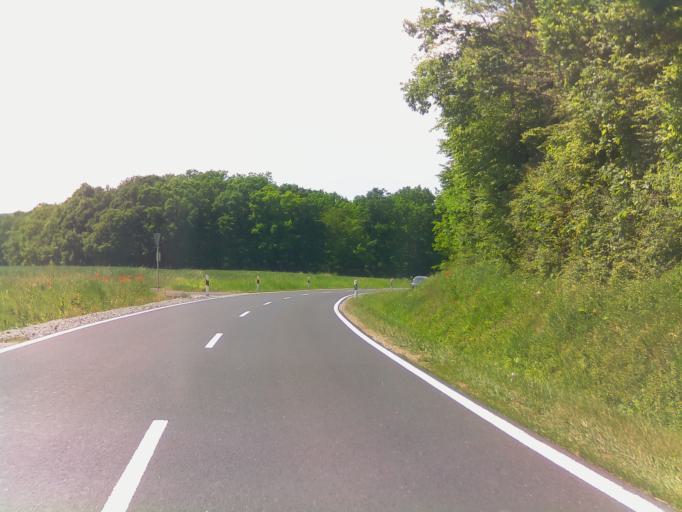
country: DE
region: Bavaria
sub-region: Regierungsbezirk Unterfranken
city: Wasserlosen
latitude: 50.0756
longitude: 10.0658
